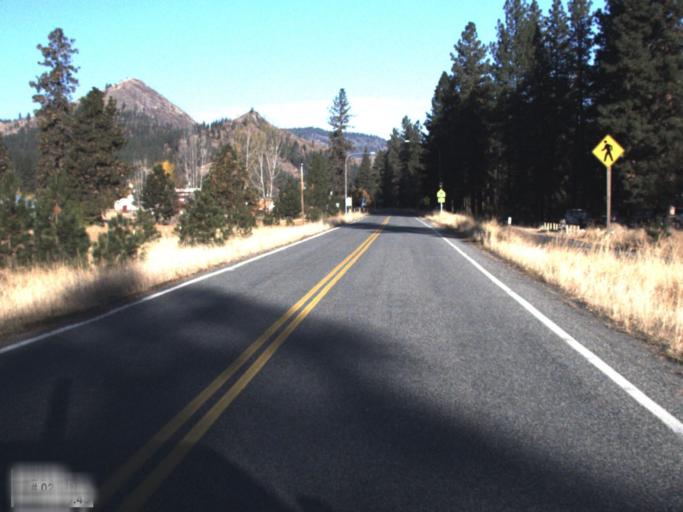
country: US
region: Washington
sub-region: Okanogan County
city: Coulee Dam
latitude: 48.0755
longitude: -118.6806
